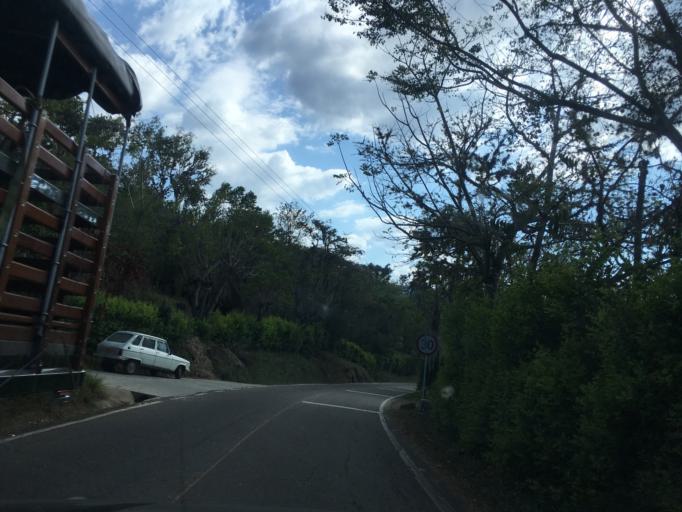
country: CO
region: Santander
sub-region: San Gil
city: San Gil
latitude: 6.5732
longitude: -73.1492
